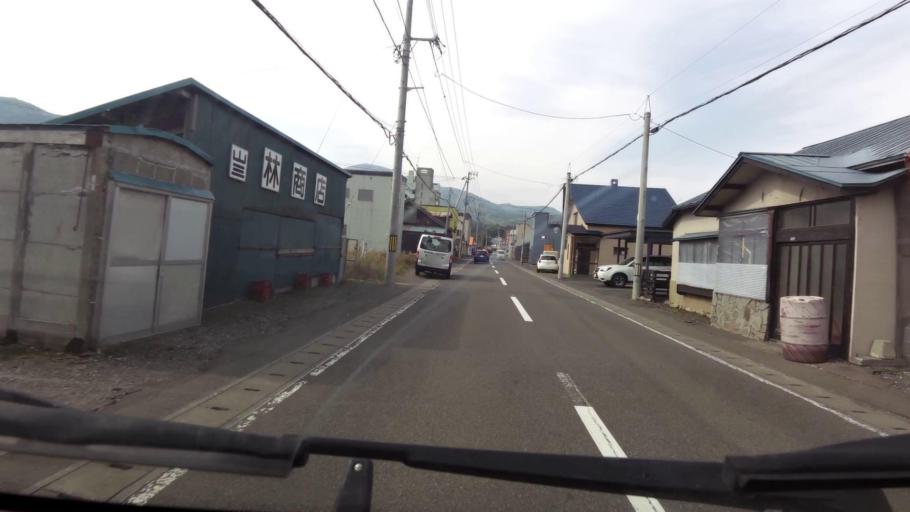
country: JP
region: Hokkaido
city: Otaru
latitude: 43.1438
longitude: 141.1639
